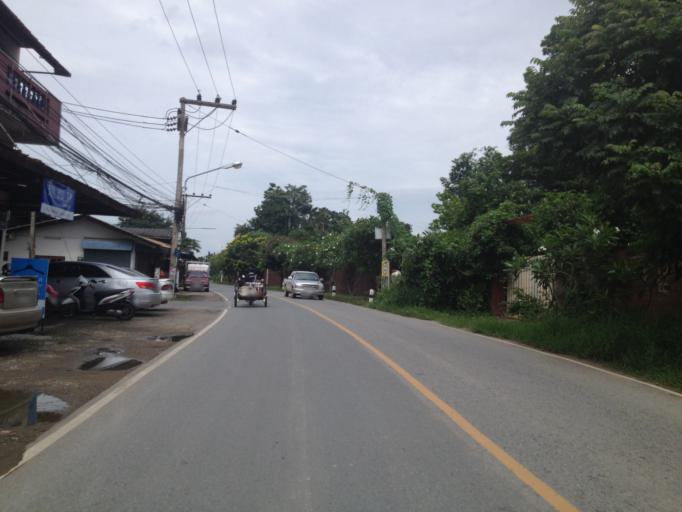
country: TH
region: Chiang Mai
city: Saraphi
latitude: 18.7132
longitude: 98.9844
